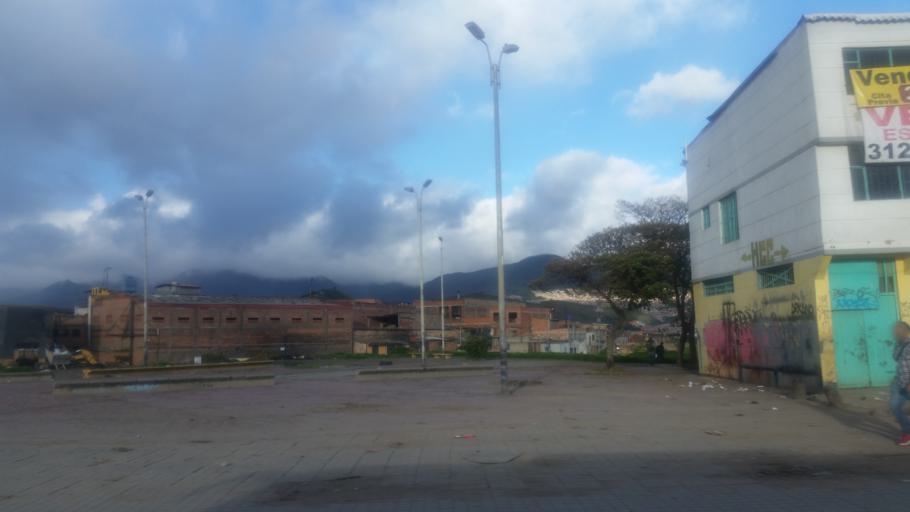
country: CO
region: Bogota D.C.
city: Bogota
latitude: 4.5630
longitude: -74.1385
